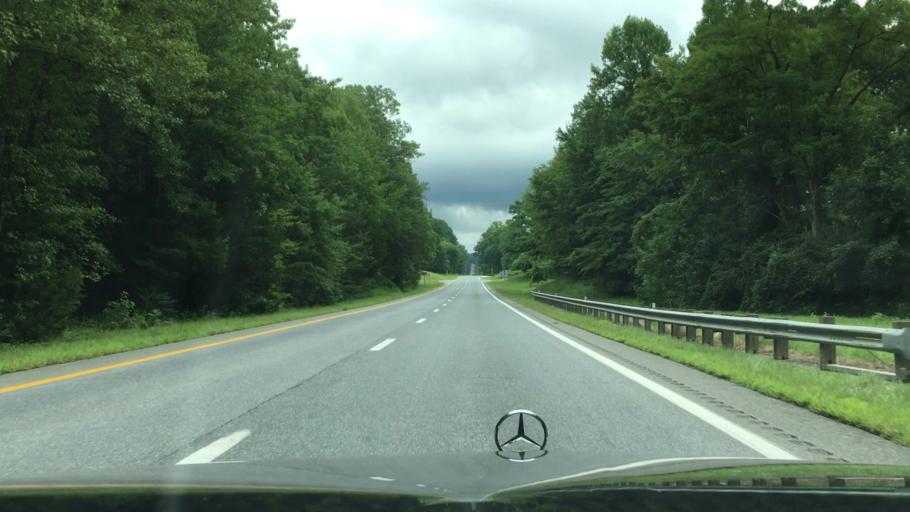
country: US
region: Virginia
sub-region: Appomattox County
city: Appomattox
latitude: 37.2746
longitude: -78.6839
